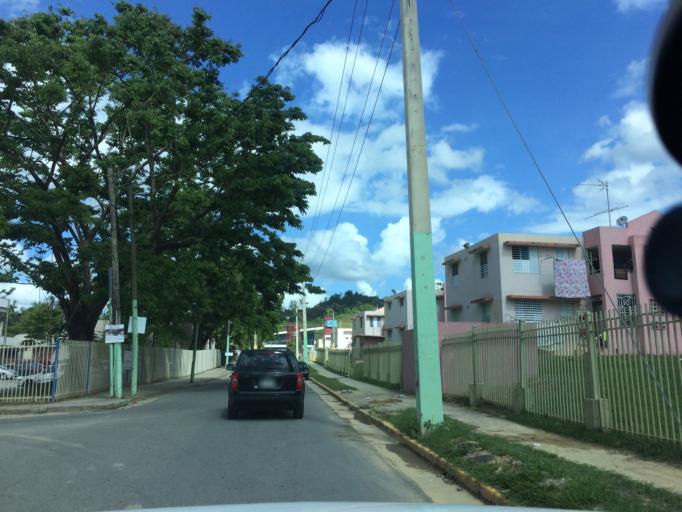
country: PR
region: Utuado
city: Utuado
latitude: 18.2671
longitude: -66.7007
